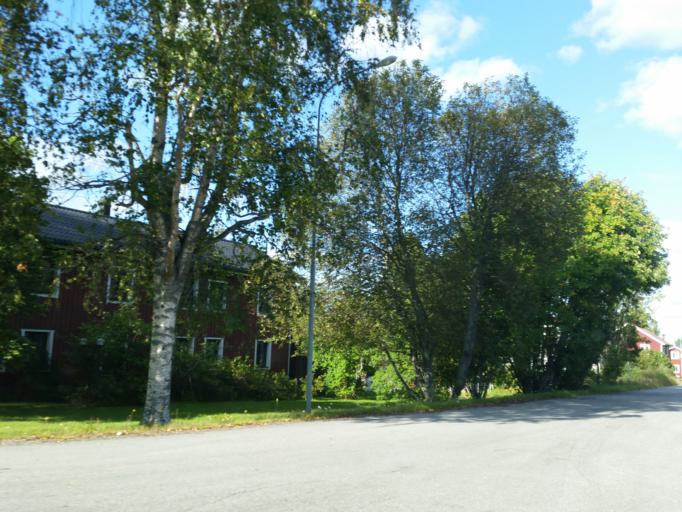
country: SE
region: Vaesterbotten
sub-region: Robertsfors Kommun
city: Robertsfors
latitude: 64.1661
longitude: 20.9309
